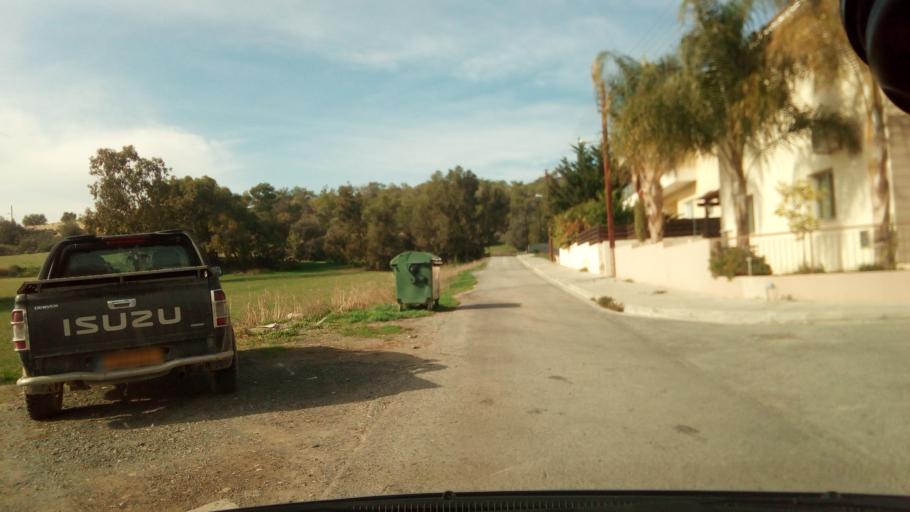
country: CY
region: Larnaka
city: Tersefanou
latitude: 34.8527
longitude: 33.4920
